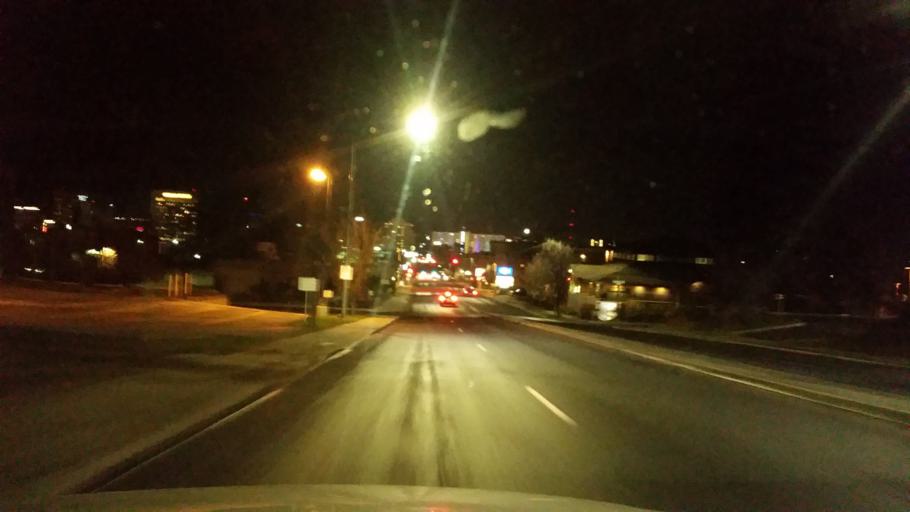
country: US
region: Washington
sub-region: Spokane County
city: Spokane
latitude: 47.6488
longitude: -117.4180
